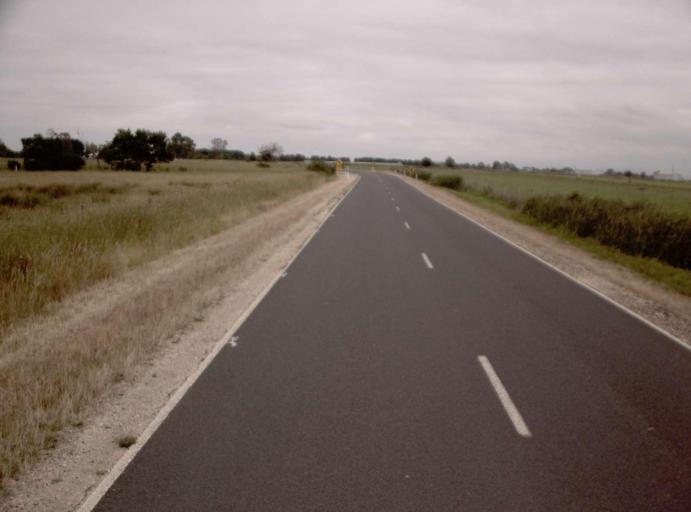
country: AU
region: Victoria
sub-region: Wellington
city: Sale
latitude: -38.0586
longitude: 146.9682
